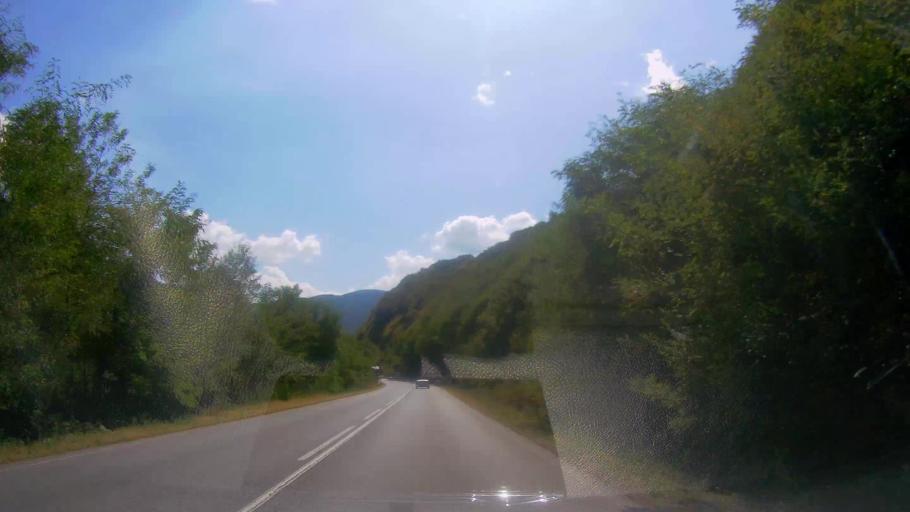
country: BG
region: Stara Zagora
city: Gurkovo
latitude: 42.7264
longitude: 25.7124
